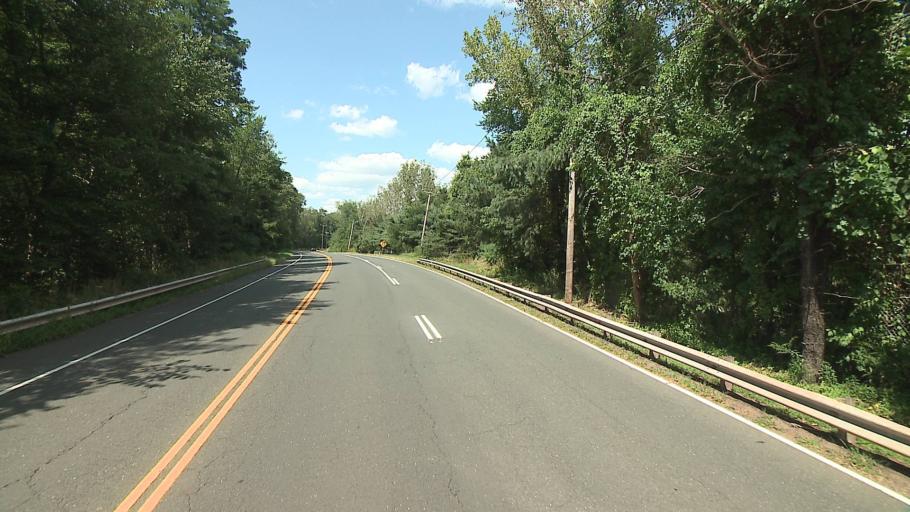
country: US
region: Connecticut
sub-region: Hartford County
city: Broad Brook
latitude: 41.9293
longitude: -72.5097
